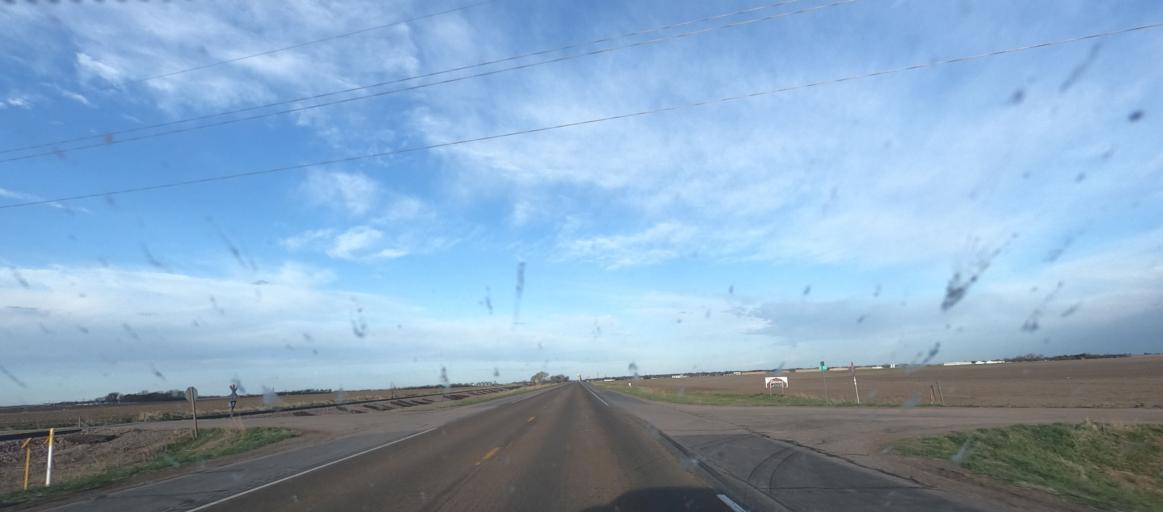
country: US
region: Nebraska
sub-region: Phelps County
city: Holdrege
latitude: 40.4469
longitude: -99.3226
